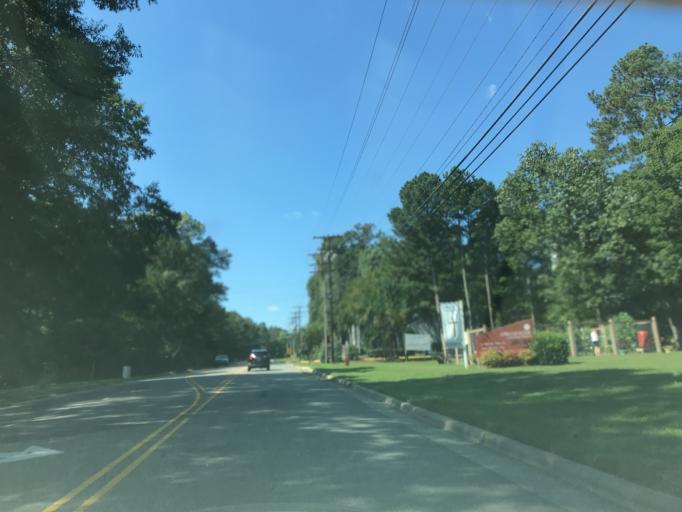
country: US
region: North Carolina
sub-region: Durham County
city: Durham
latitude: 35.9027
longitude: -78.9042
